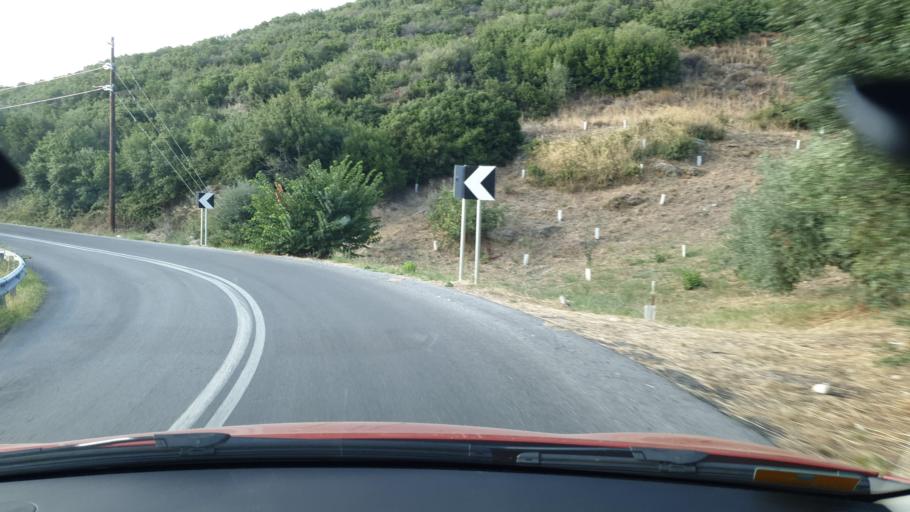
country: GR
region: Thessaly
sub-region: Nomos Magnisias
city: Pteleos
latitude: 39.0647
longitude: 22.9273
